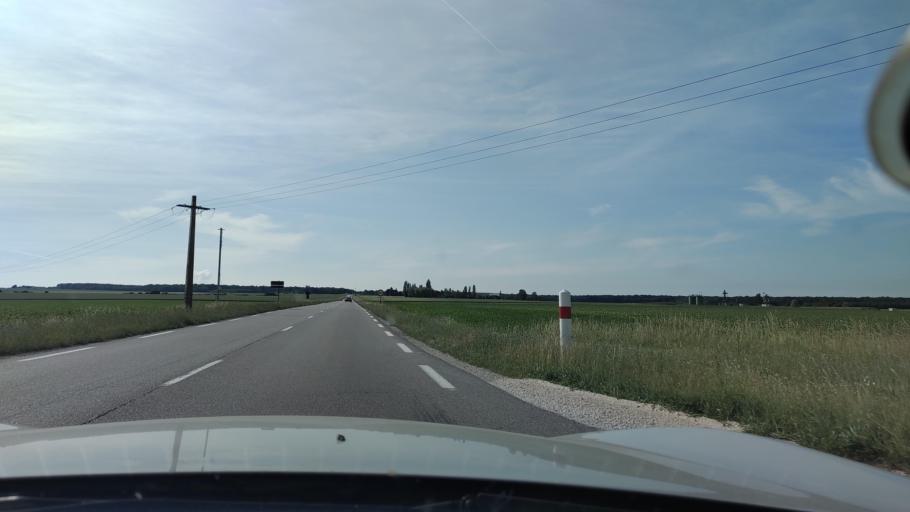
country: FR
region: Ile-de-France
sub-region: Departement de Seine-et-Marne
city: Jouy-le-Chatel
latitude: 48.6556
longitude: 3.1493
